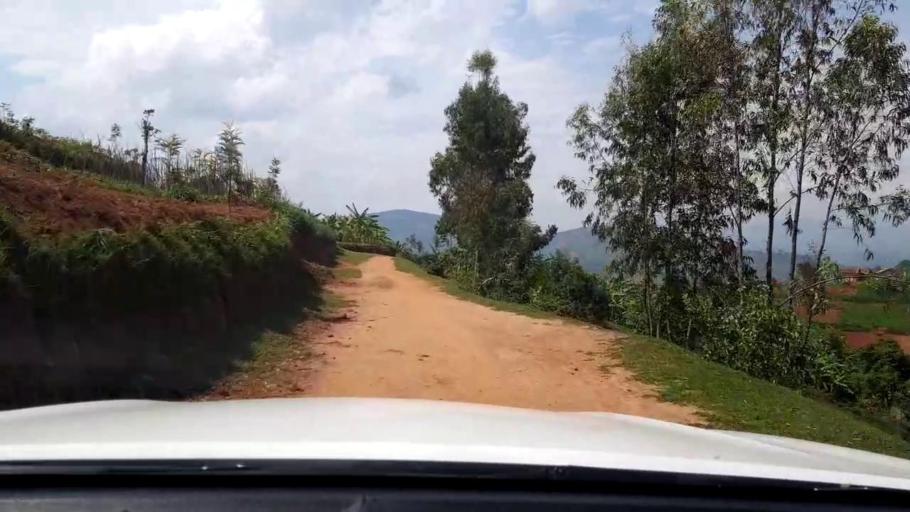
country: RW
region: Southern Province
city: Gitarama
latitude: -2.0561
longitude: 29.6700
